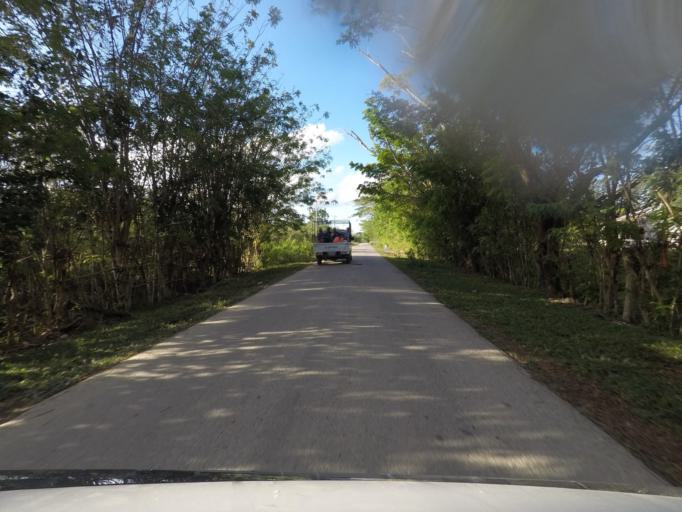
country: TL
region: Lautem
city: Lospalos
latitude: -8.4626
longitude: 126.9970
